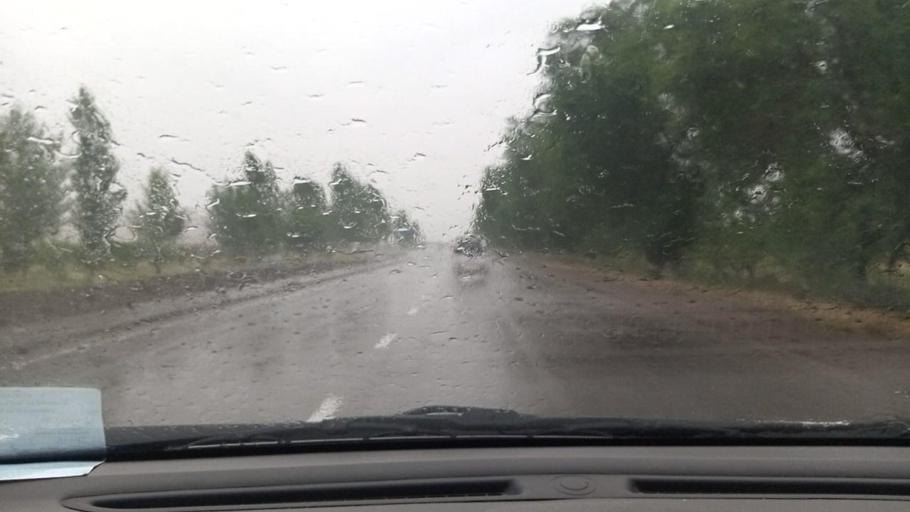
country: UZ
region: Toshkent
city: Ohangaron
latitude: 40.9273
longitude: 69.8512
